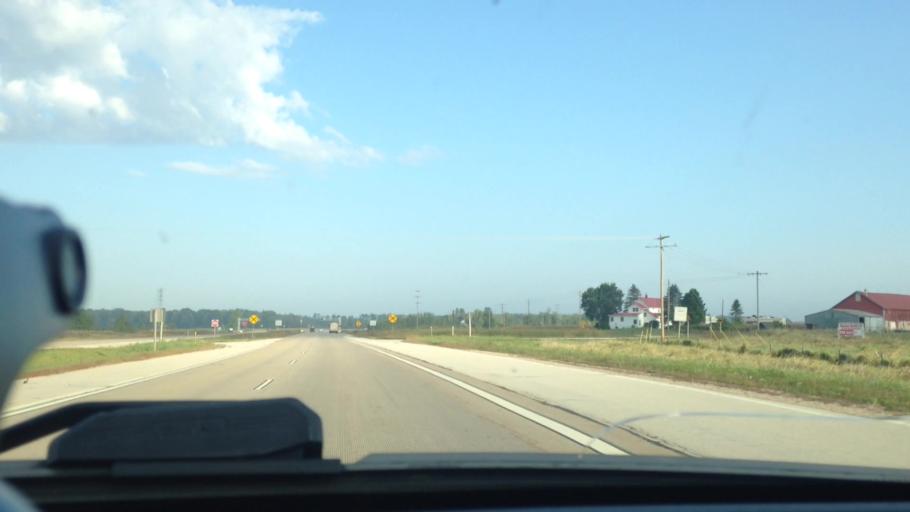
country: US
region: Wisconsin
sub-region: Oconto County
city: Oconto Falls
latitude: 44.9793
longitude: -88.0436
